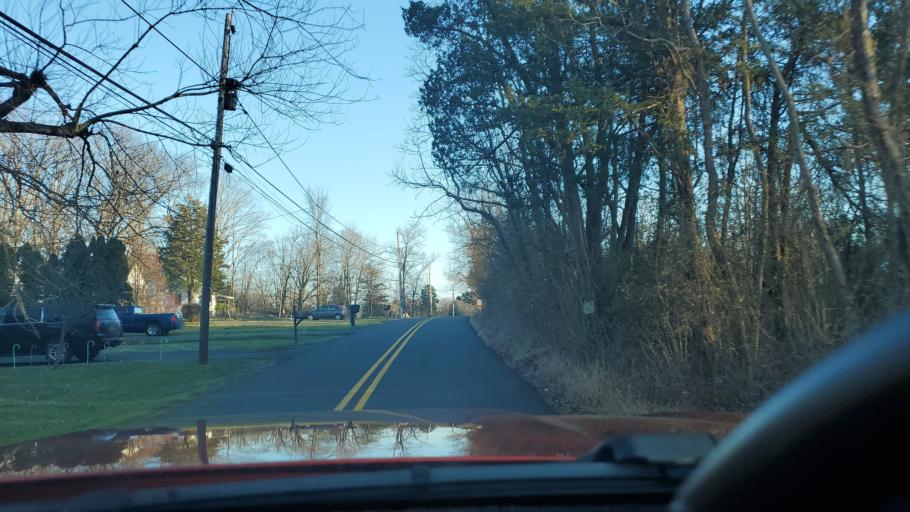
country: US
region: Pennsylvania
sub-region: Montgomery County
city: Woxall
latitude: 40.3102
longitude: -75.4902
